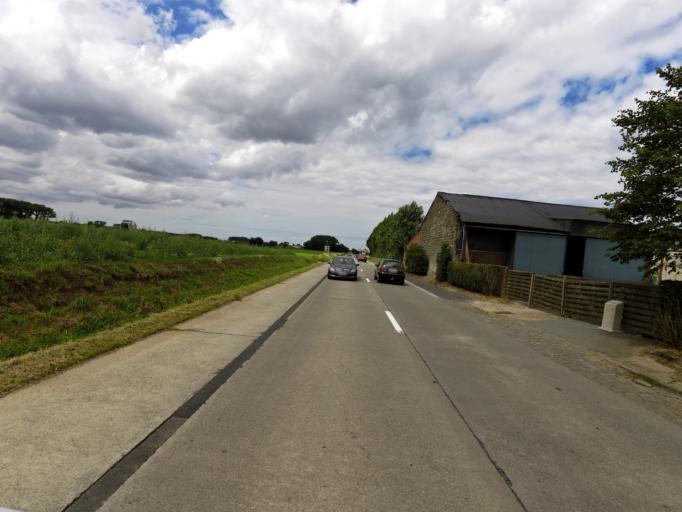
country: BE
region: Flanders
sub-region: Provincie West-Vlaanderen
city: Ichtegem
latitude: 51.0628
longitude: 3.0028
